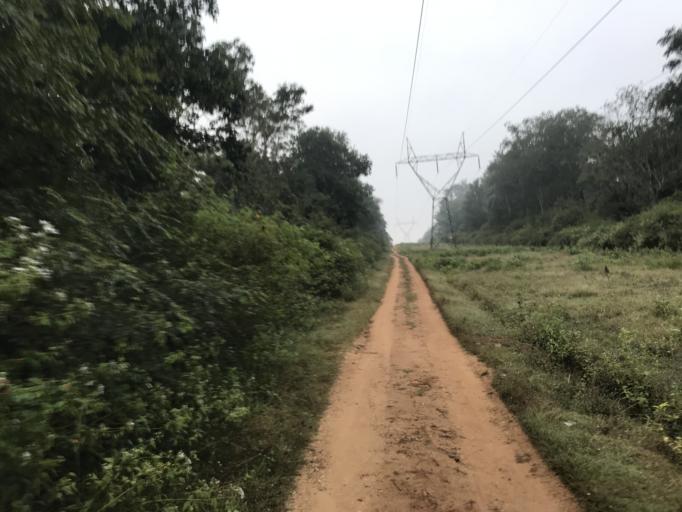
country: IN
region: Karnataka
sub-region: Mysore
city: Heggadadevankote
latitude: 11.9649
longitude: 76.2161
